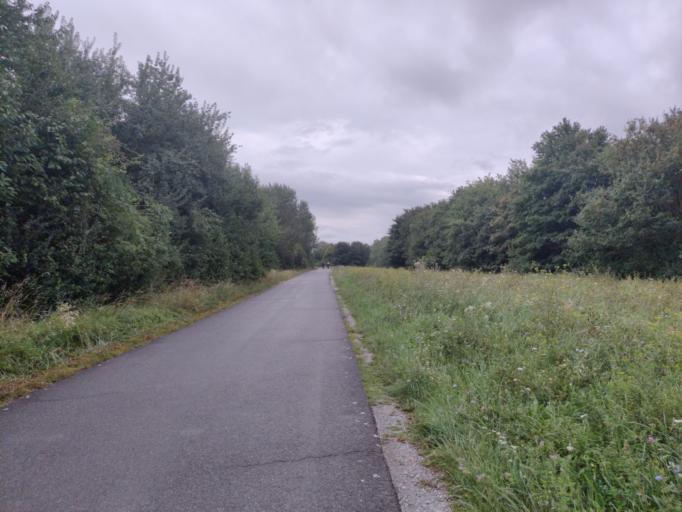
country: AT
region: Lower Austria
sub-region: Politischer Bezirk Korneuburg
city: Langenzersdorf
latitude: 48.2854
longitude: 16.3551
